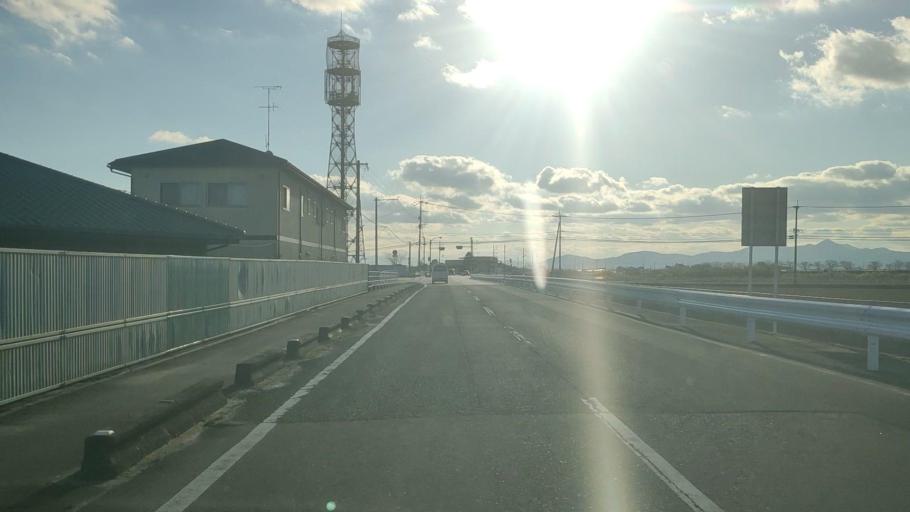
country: JP
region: Saga Prefecture
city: Saga-shi
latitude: 33.3044
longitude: 130.2554
